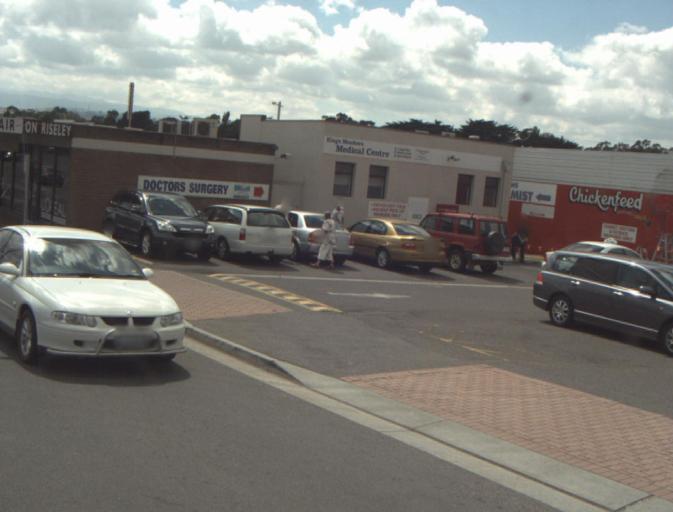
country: AU
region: Tasmania
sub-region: Launceston
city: East Launceston
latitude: -41.4653
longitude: 147.1581
